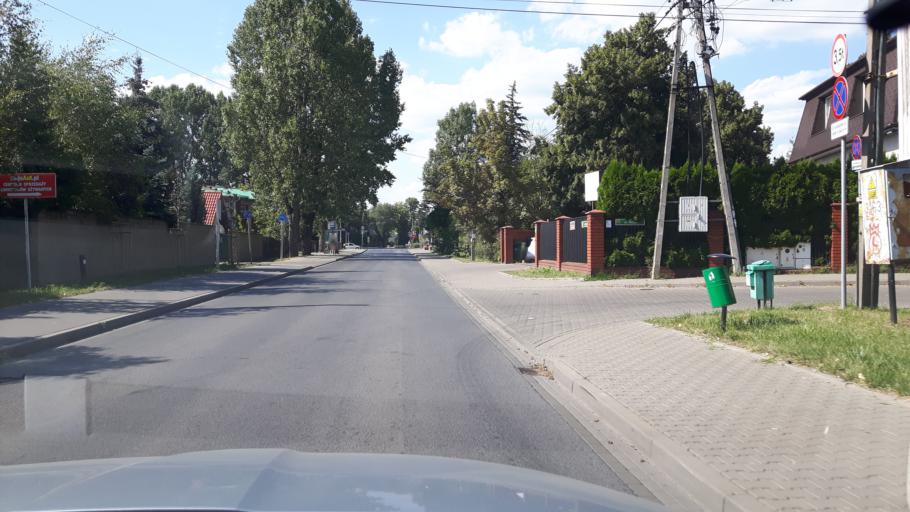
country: PL
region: Masovian Voivodeship
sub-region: Powiat pruszkowski
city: Nowe Grocholice
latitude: 52.1802
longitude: 20.9060
